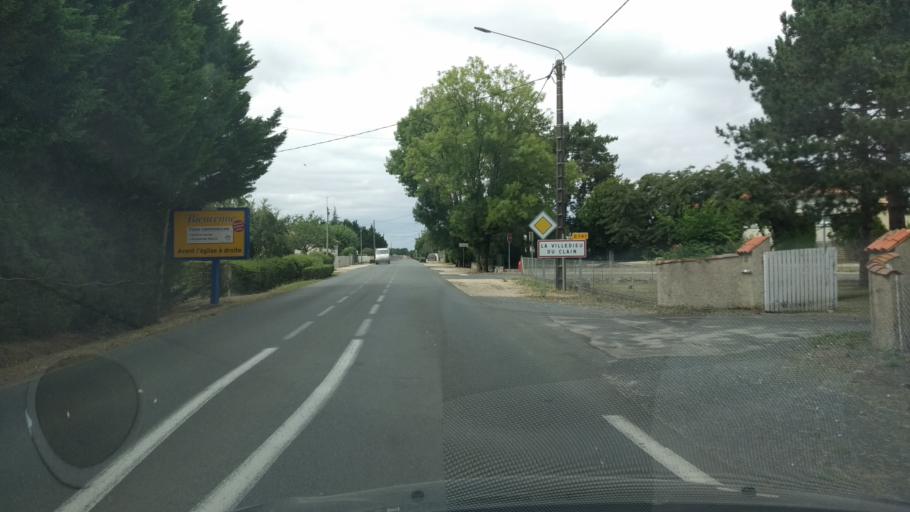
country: FR
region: Poitou-Charentes
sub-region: Departement de la Vienne
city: La Villedieu-du-Clain
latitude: 46.4487
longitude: 0.3688
